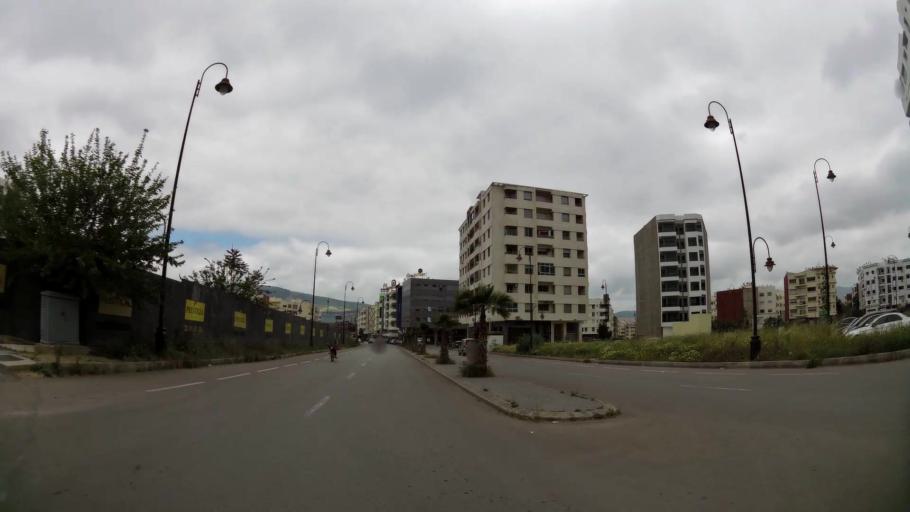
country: MA
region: Fes-Boulemane
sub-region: Fes
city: Fes
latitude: 34.0374
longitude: -5.0111
